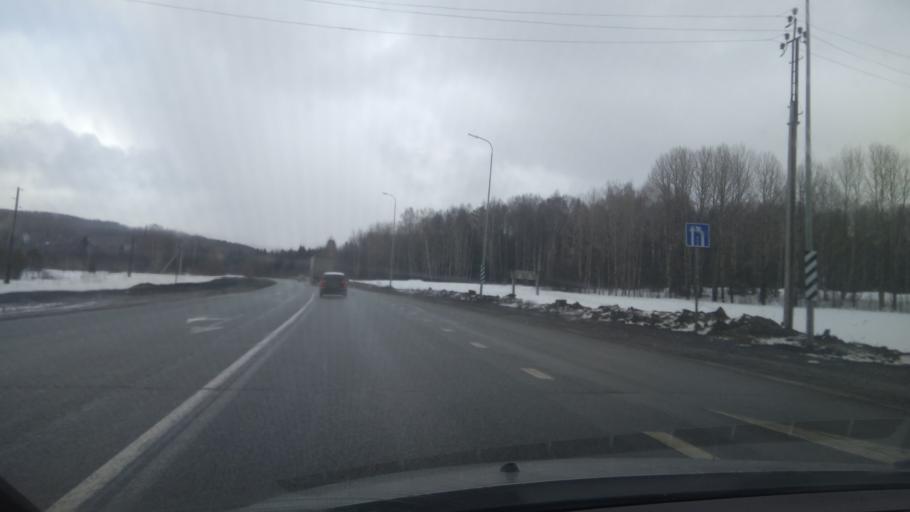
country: RU
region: Sverdlovsk
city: Ufimskiy
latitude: 56.7812
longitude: 58.4046
